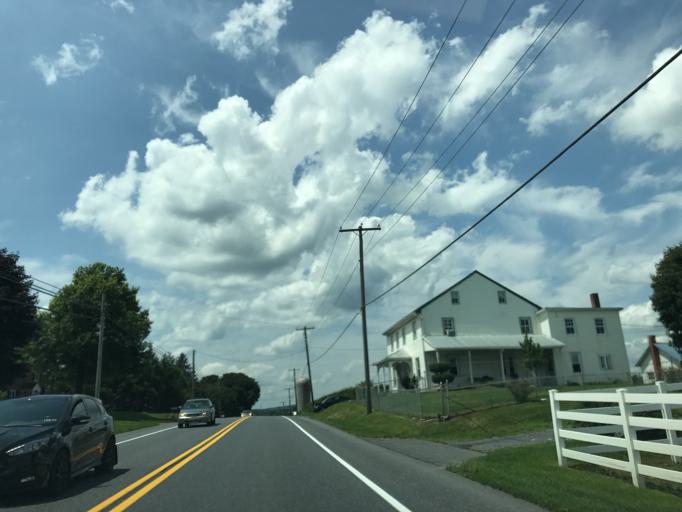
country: US
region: Pennsylvania
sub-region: Lancaster County
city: Clay
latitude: 40.2103
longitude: -76.2296
